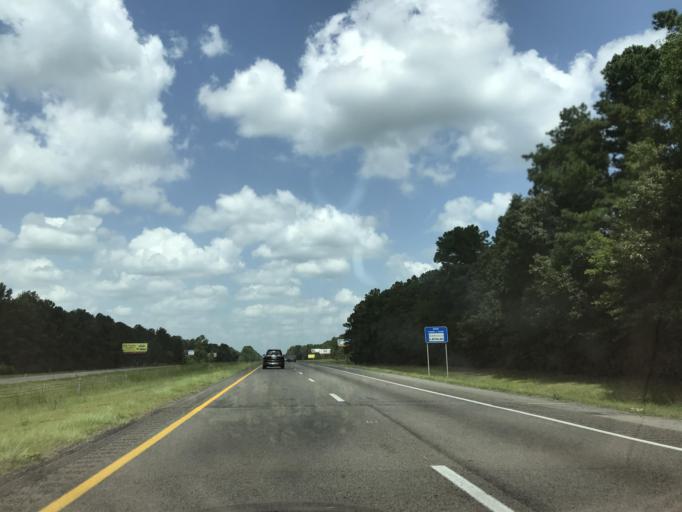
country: US
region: North Carolina
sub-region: Pender County
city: Burgaw
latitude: 34.6461
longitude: -77.9399
